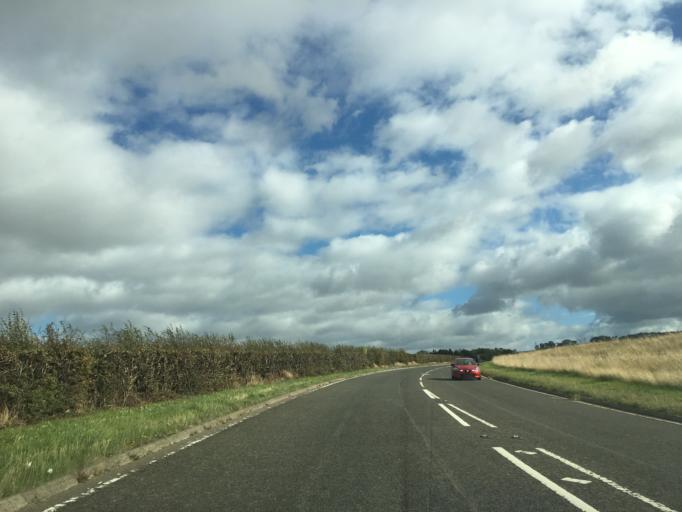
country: GB
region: Scotland
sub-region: Midlothian
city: Dalkeith
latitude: 55.8914
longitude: -3.0340
